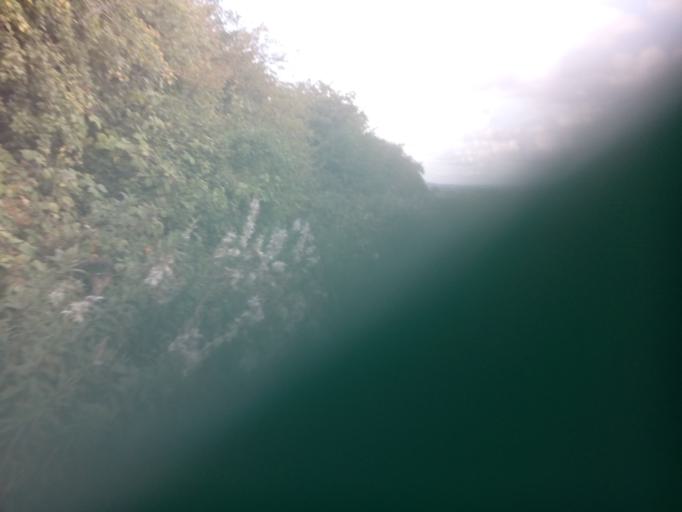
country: GB
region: England
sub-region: County Durham
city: West Rainton
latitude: 54.7882
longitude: -1.5160
